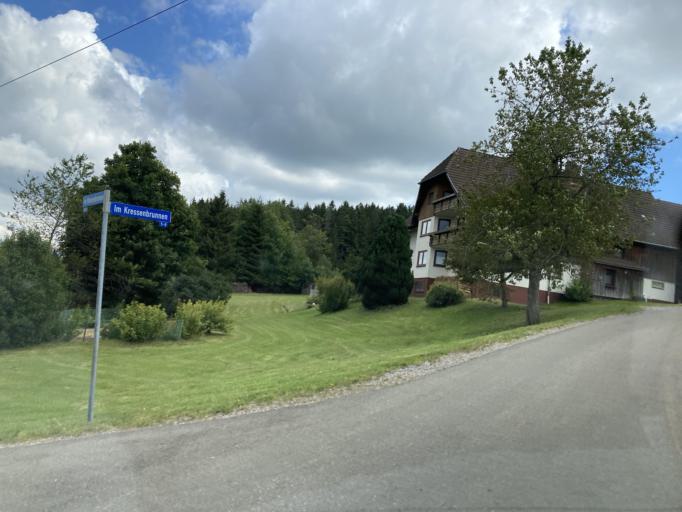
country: DE
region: Baden-Wuerttemberg
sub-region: Freiburg Region
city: Sankt Georgen im Schwarzwald
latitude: 48.1050
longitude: 8.3391
